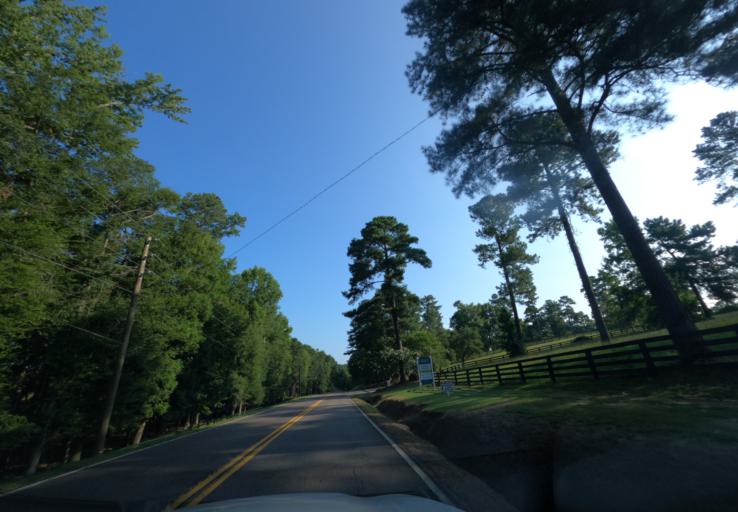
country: US
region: South Carolina
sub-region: Edgefield County
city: Murphys Estates
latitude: 33.6707
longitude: -81.9784
